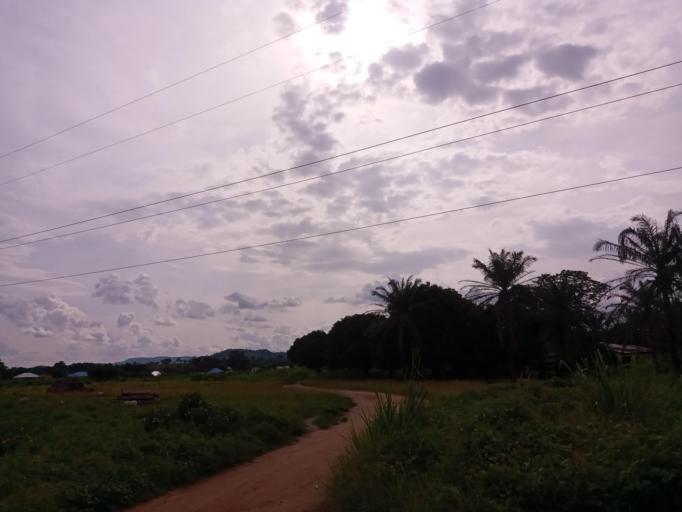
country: SL
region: Northern Province
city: Bumbuna
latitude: 9.0491
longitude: -11.7525
